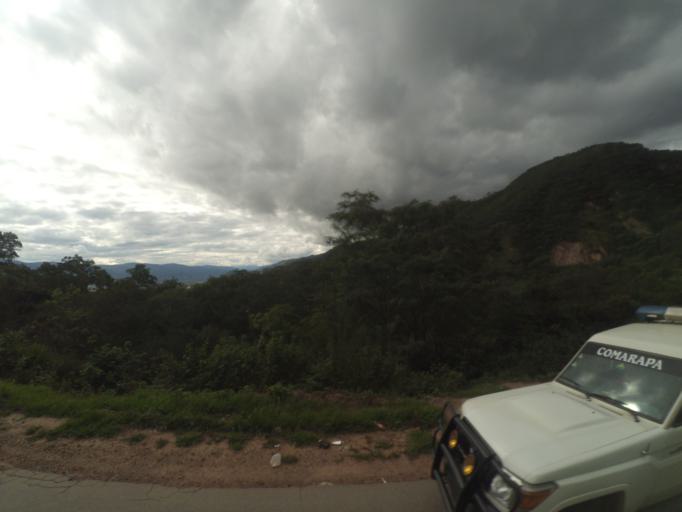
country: BO
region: Santa Cruz
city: Samaipata
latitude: -18.1673
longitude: -63.8936
